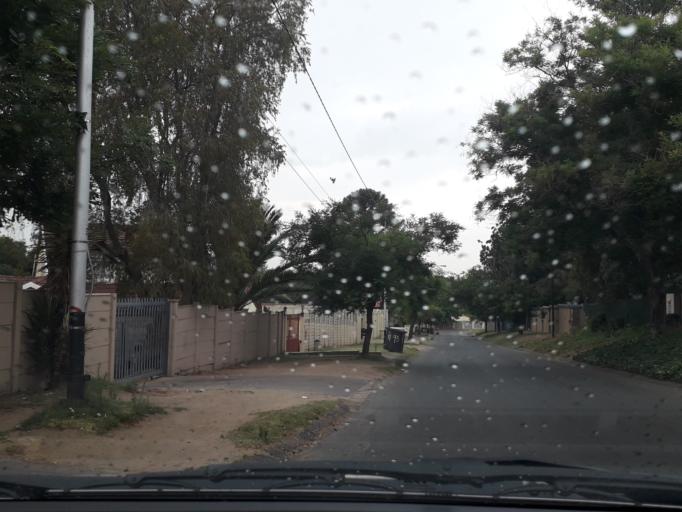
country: ZA
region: Gauteng
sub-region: City of Johannesburg Metropolitan Municipality
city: Modderfontein
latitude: -26.1323
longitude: 28.1044
